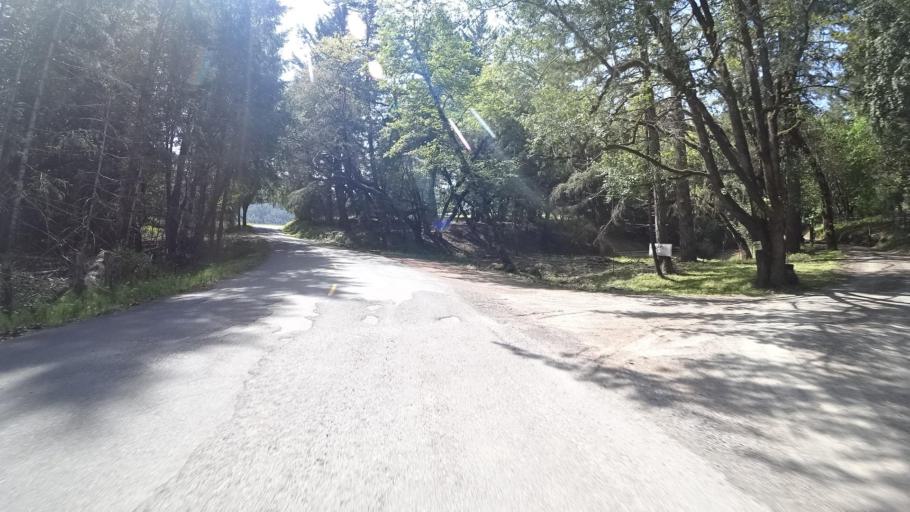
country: US
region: California
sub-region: Humboldt County
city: Redway
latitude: 40.3903
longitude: -123.7440
